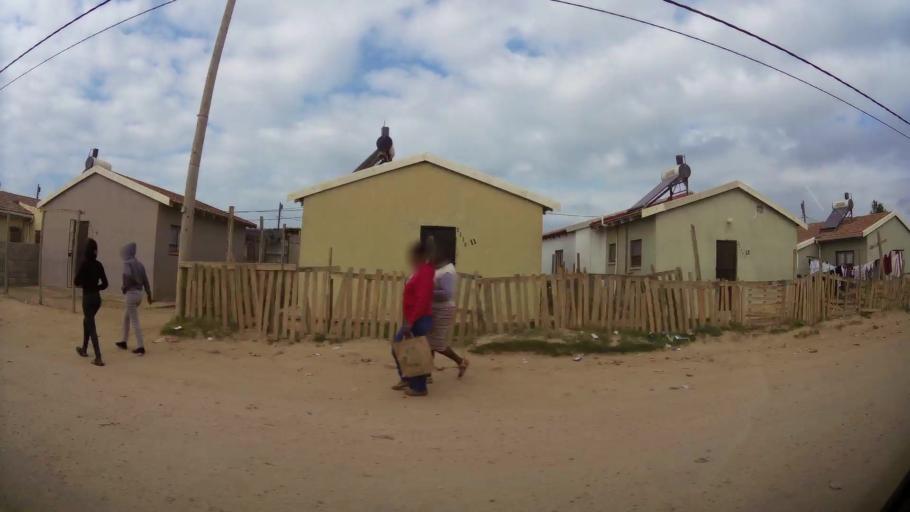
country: ZA
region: Eastern Cape
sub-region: Nelson Mandela Bay Metropolitan Municipality
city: Port Elizabeth
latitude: -33.8300
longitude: 25.6294
